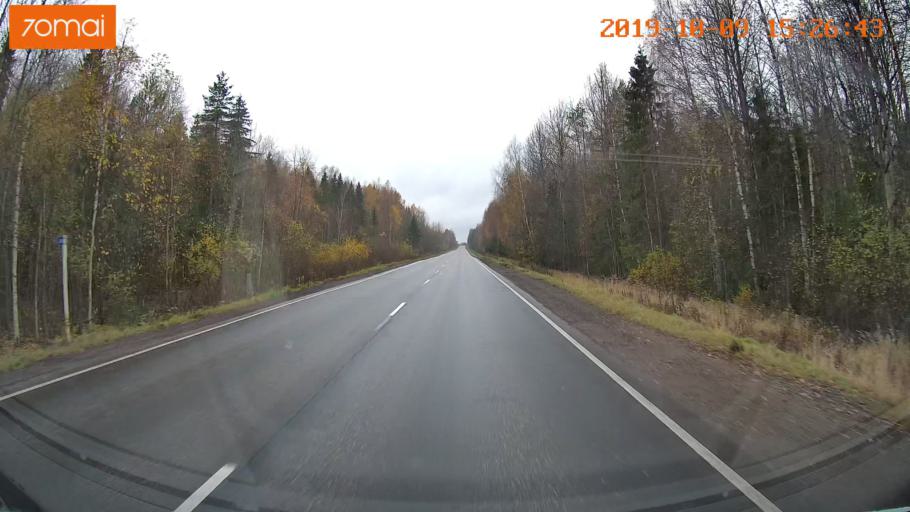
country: RU
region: Kostroma
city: Susanino
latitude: 58.0183
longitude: 41.3971
